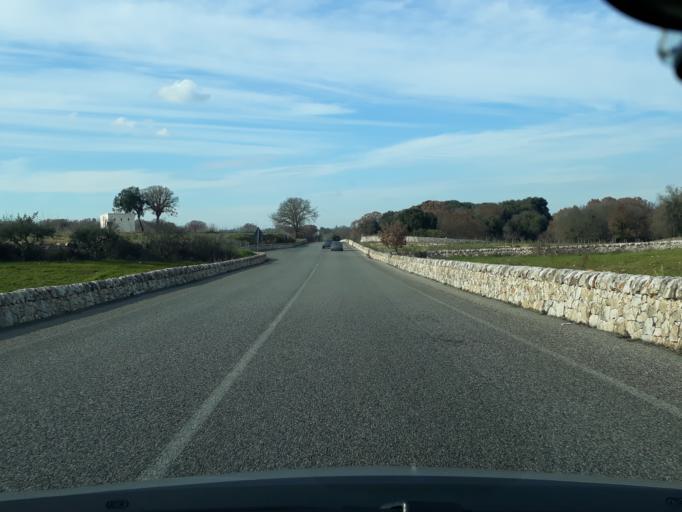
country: IT
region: Apulia
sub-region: Provincia di Bari
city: Locorotondo
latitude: 40.7586
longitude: 17.3408
